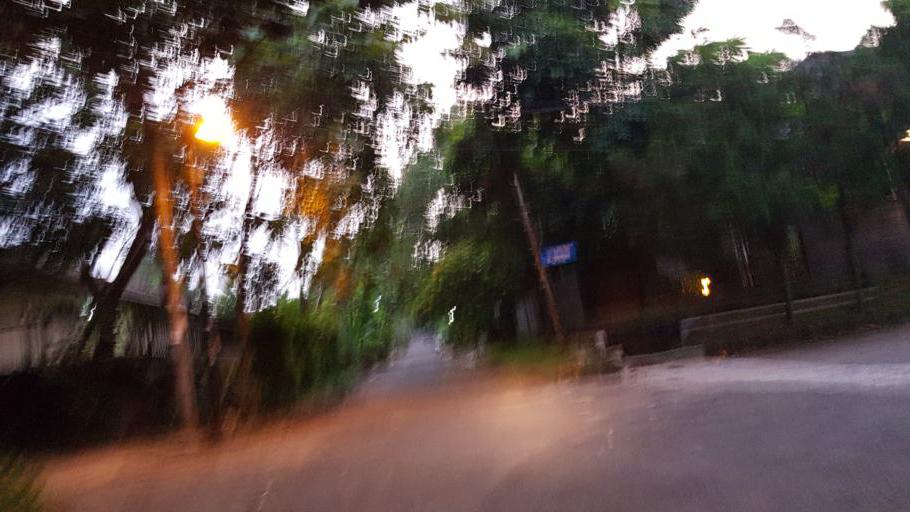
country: ID
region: West Java
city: Pamulang
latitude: -6.3436
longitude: 106.7812
